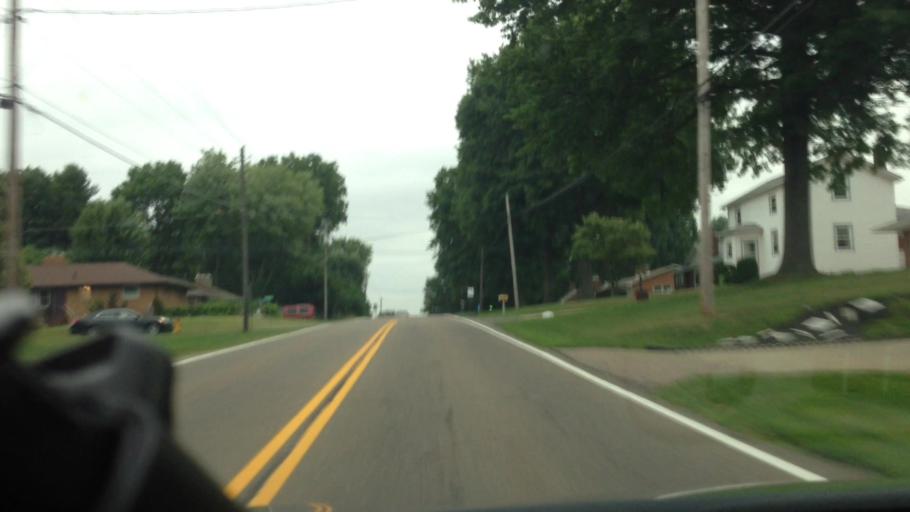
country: US
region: Ohio
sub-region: Stark County
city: Massillon
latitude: 40.8258
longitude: -81.5126
